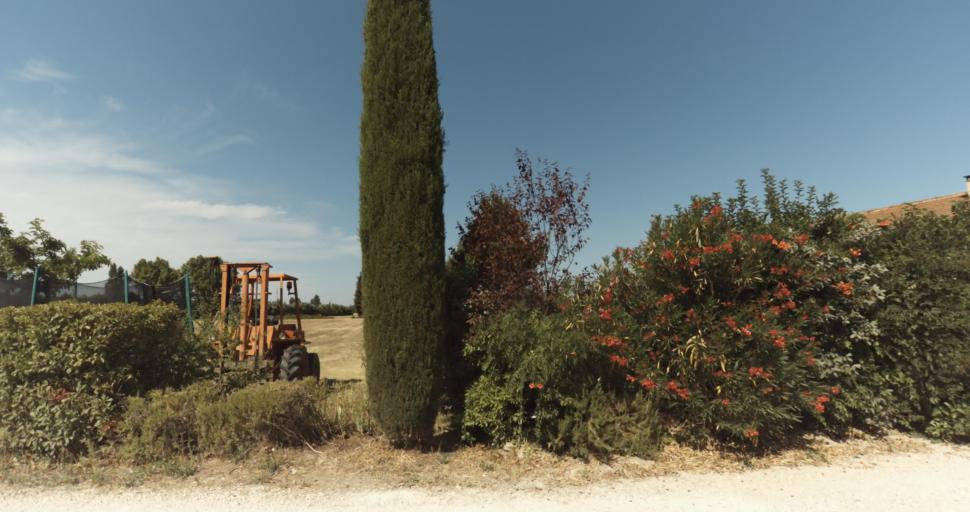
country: FR
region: Provence-Alpes-Cote d'Azur
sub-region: Departement du Vaucluse
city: Monteux
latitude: 44.0178
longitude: 4.9950
